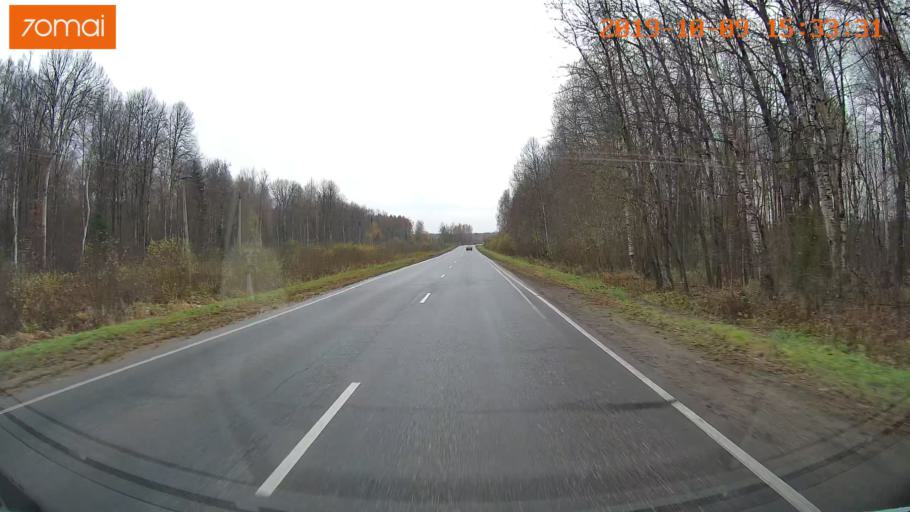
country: RU
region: Kostroma
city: Oktyabr'skiy
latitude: 57.9506
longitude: 41.2613
